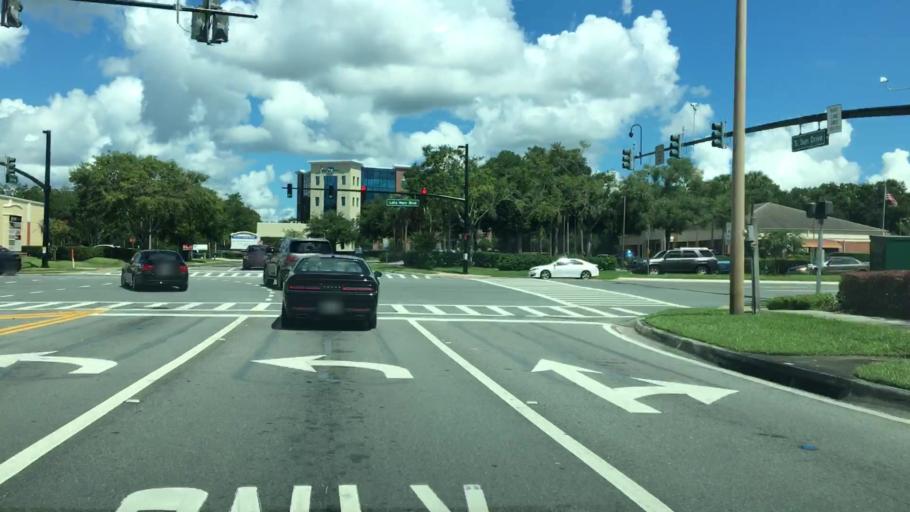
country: US
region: Florida
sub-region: Seminole County
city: Heathrow
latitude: 28.7558
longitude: -81.3524
